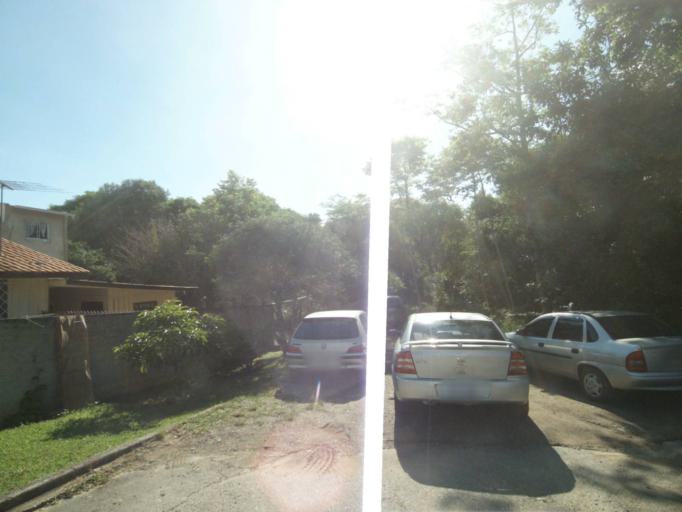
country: BR
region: Parana
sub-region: Curitiba
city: Curitiba
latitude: -25.4405
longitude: -49.3252
